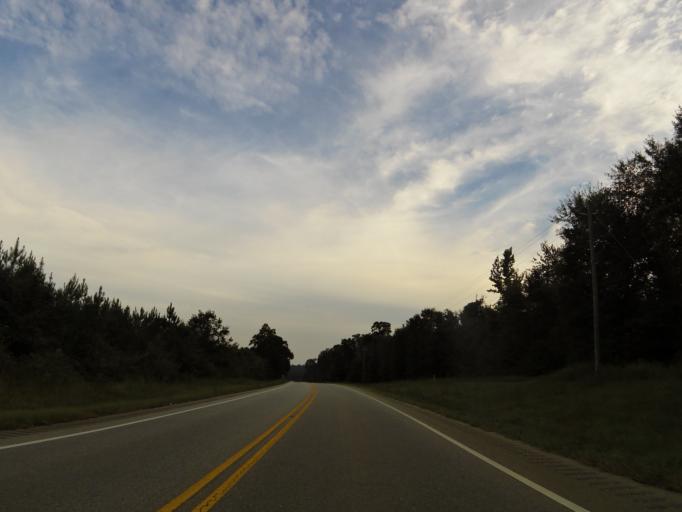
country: US
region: Alabama
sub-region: Monroe County
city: Frisco City
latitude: 31.2701
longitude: -87.5006
